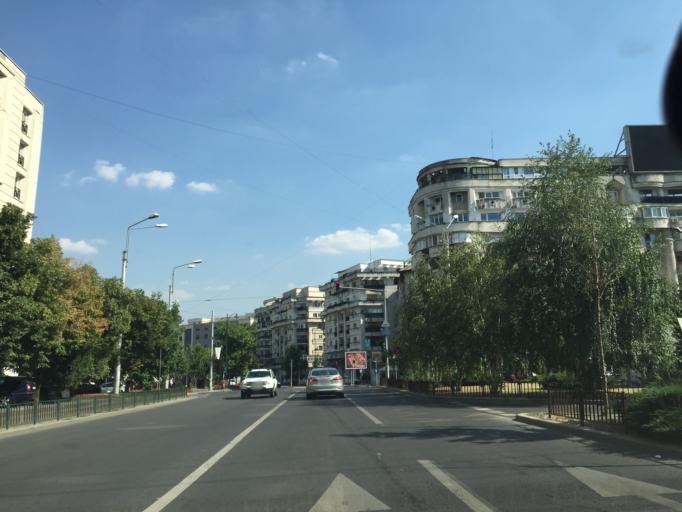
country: RO
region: Bucuresti
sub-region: Municipiul Bucuresti
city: Bucharest
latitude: 44.4294
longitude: 26.1077
